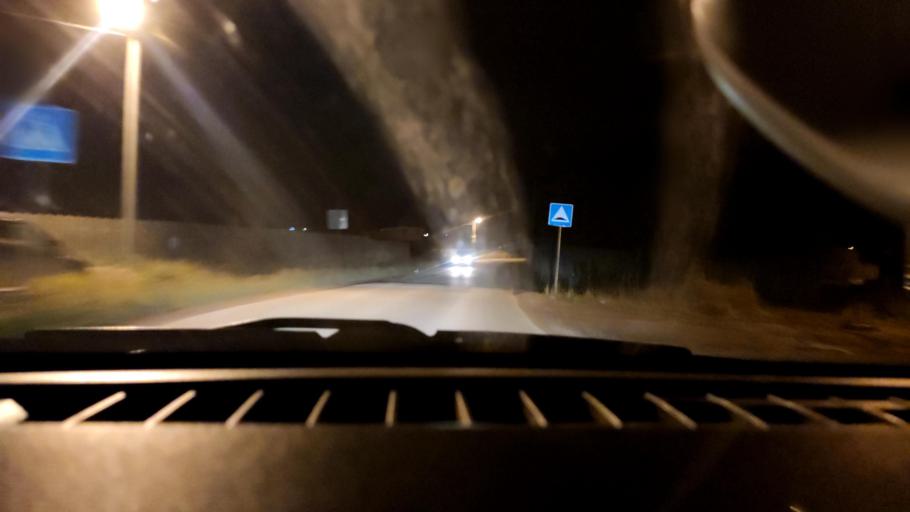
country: RU
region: Perm
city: Ferma
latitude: 57.9073
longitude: 56.3049
